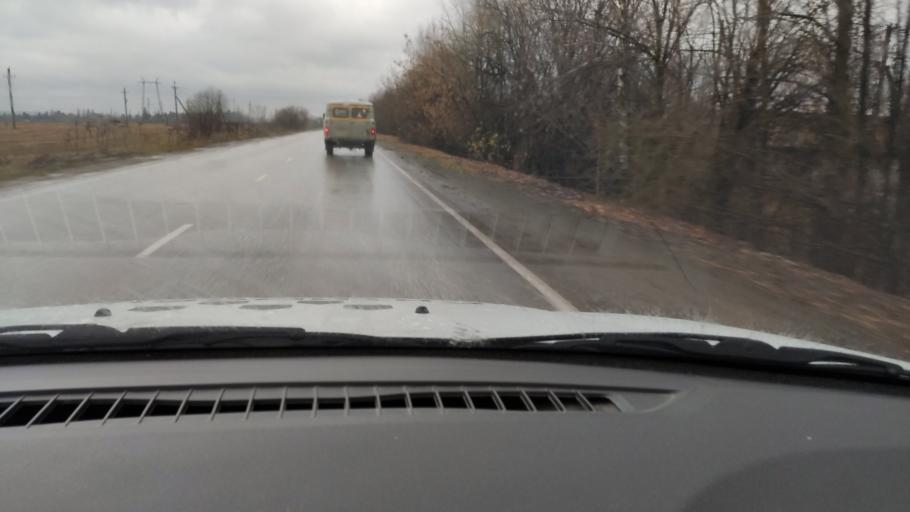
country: RU
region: Perm
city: Sylva
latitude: 58.0283
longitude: 56.7106
